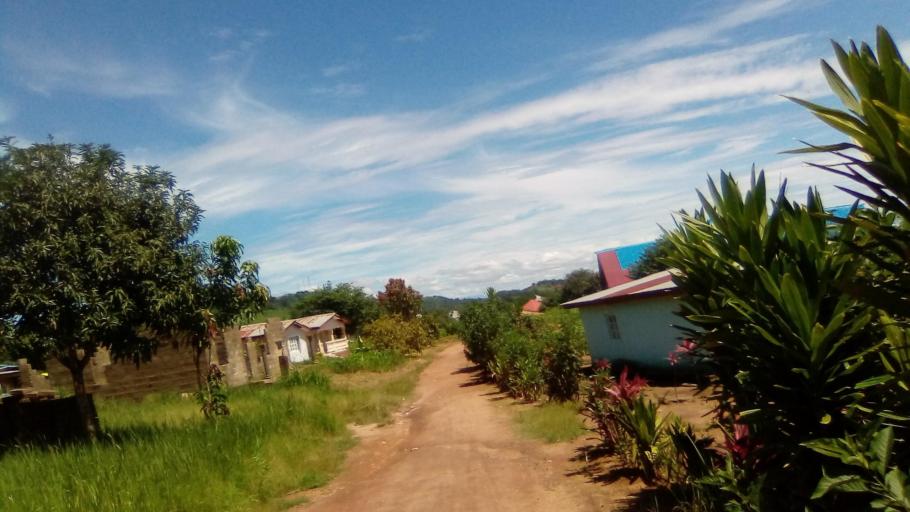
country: SL
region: Eastern Province
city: Simbakoro
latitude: 8.6315
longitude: -10.9981
